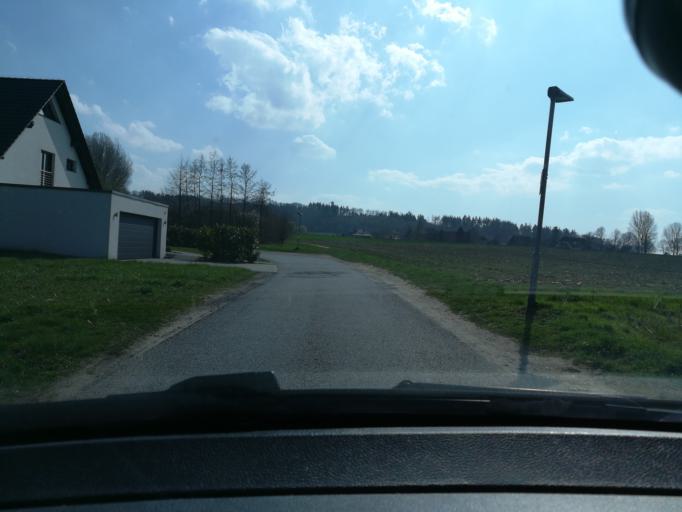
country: DE
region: North Rhine-Westphalia
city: Borgholzhausen
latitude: 52.0981
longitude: 8.3020
